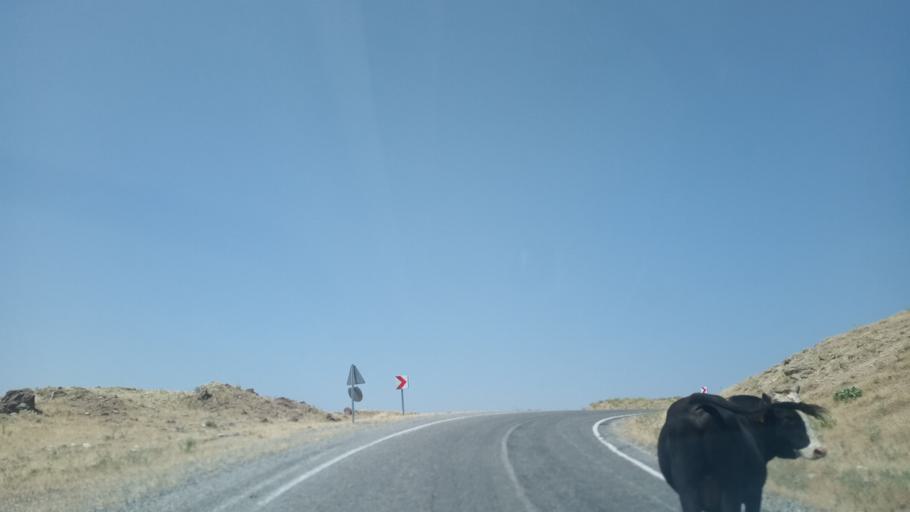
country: TR
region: Siirt
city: Dilektepe
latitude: 38.0654
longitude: 41.8317
